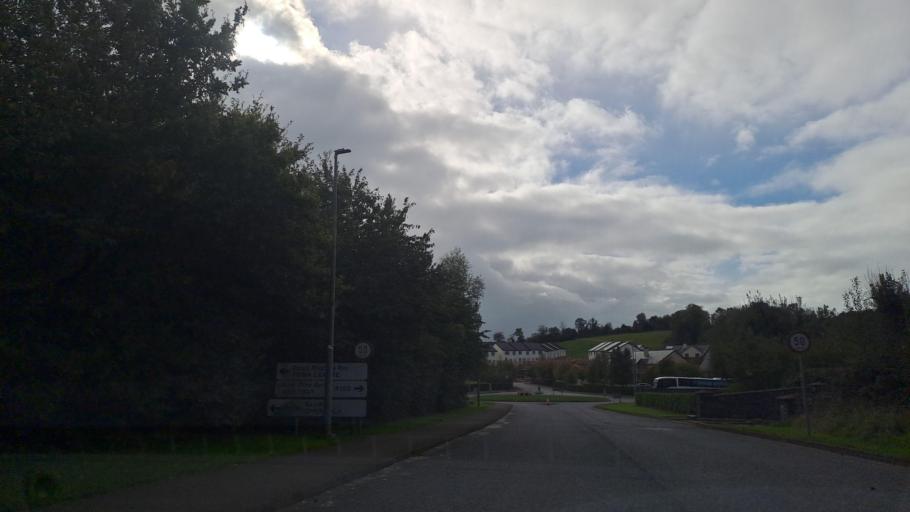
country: IE
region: Ulster
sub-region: County Monaghan
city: Carrickmacross
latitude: 53.9881
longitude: -6.7220
